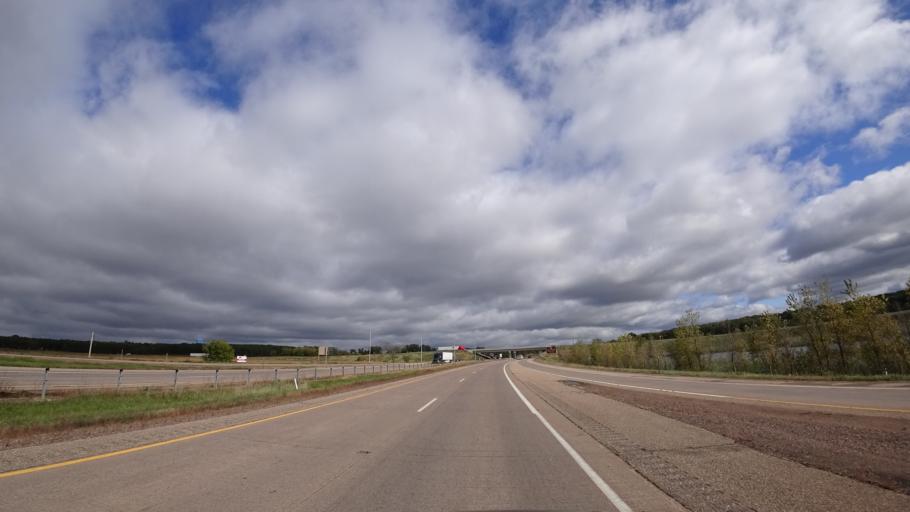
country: US
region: Wisconsin
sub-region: Chippewa County
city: Chippewa Falls
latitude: 44.9194
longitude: -91.3621
